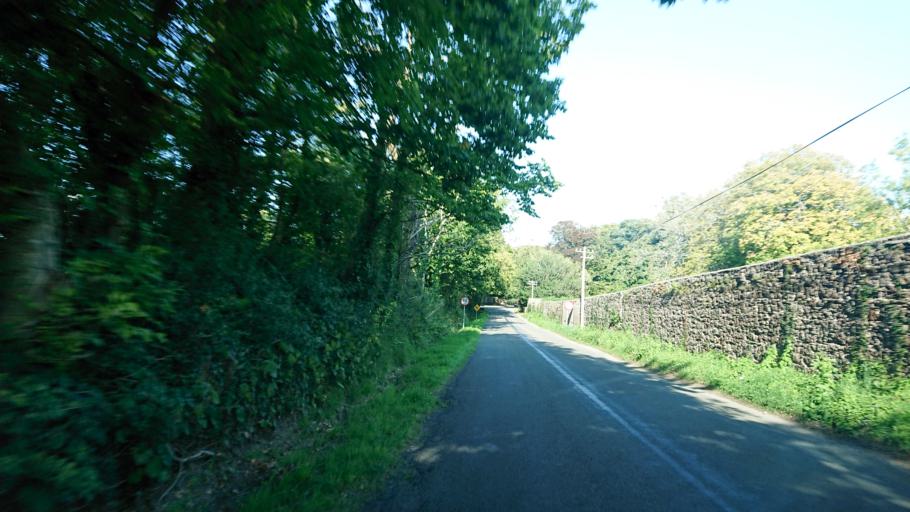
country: IE
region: Munster
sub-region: Waterford
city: Dunmore East
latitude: 52.1910
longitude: -6.9864
